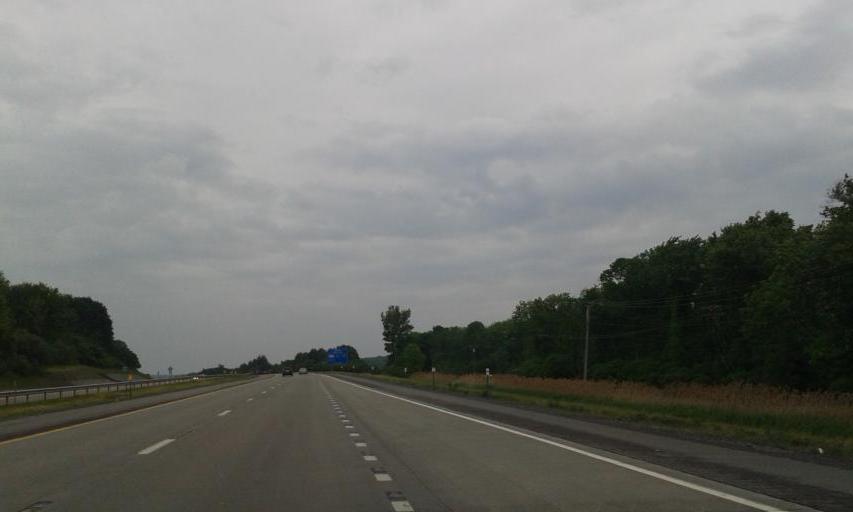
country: US
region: New York
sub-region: Onondaga County
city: Seneca Knolls
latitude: 43.1057
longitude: -76.2932
